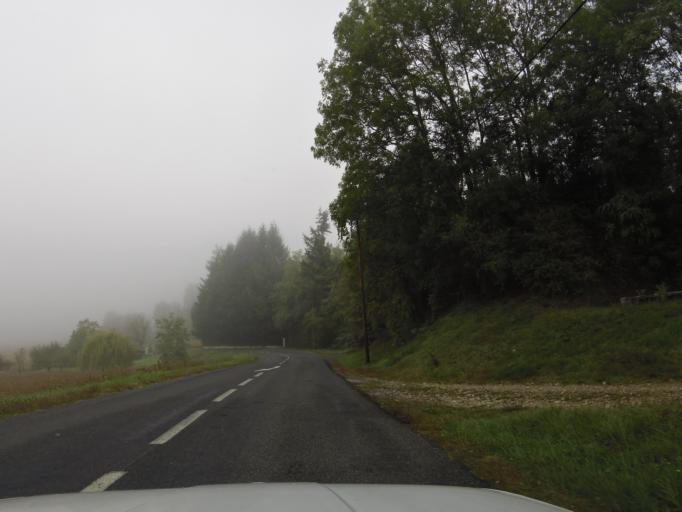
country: FR
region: Rhone-Alpes
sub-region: Departement de l'Isere
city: Creys-Mepieu
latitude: 45.7798
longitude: 5.4696
